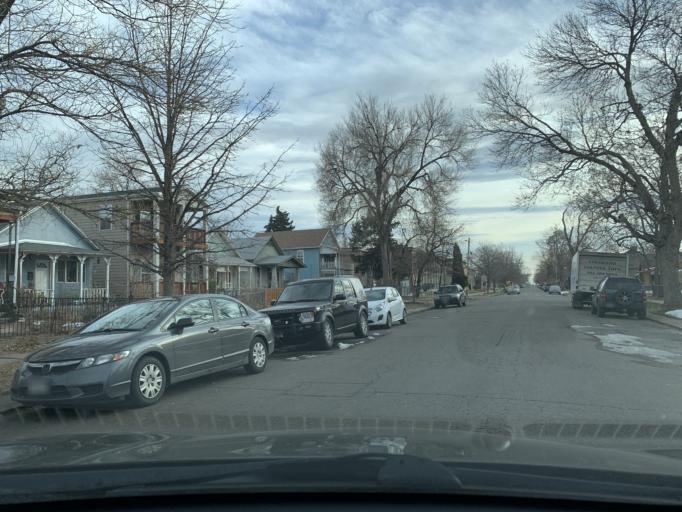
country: US
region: Colorado
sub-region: Denver County
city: Denver
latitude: 39.7360
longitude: -105.0016
